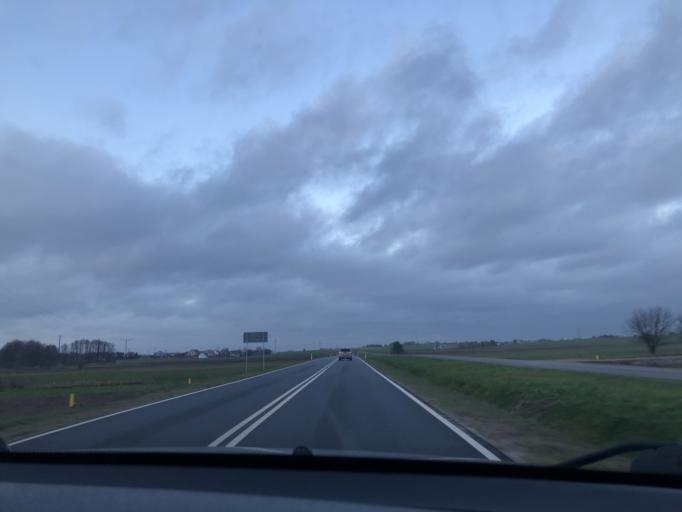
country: PL
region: Podlasie
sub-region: Lomza
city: Lomza
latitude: 53.1371
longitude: 22.0506
